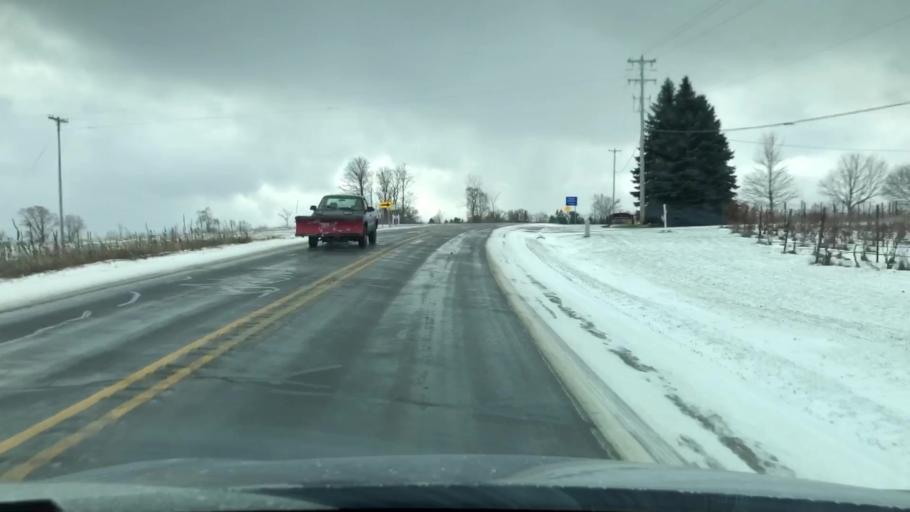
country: US
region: Michigan
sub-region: Antrim County
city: Elk Rapids
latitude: 44.8657
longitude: -85.5168
